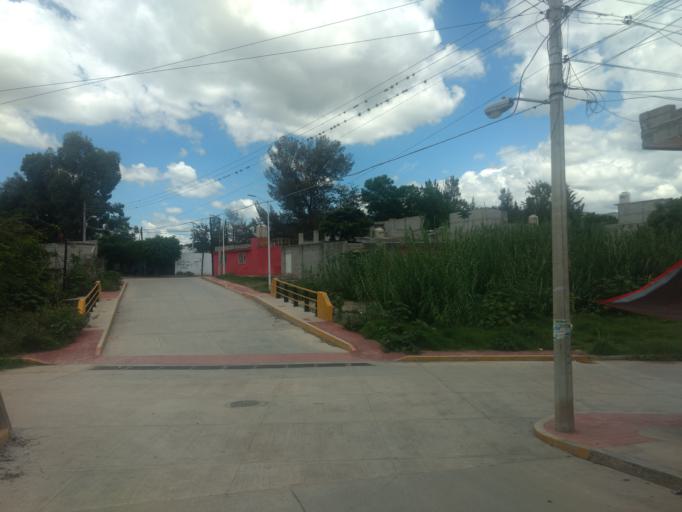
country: MX
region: Oaxaca
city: Ciudad de Huajuapam de Leon
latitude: 17.8142
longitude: -97.7689
